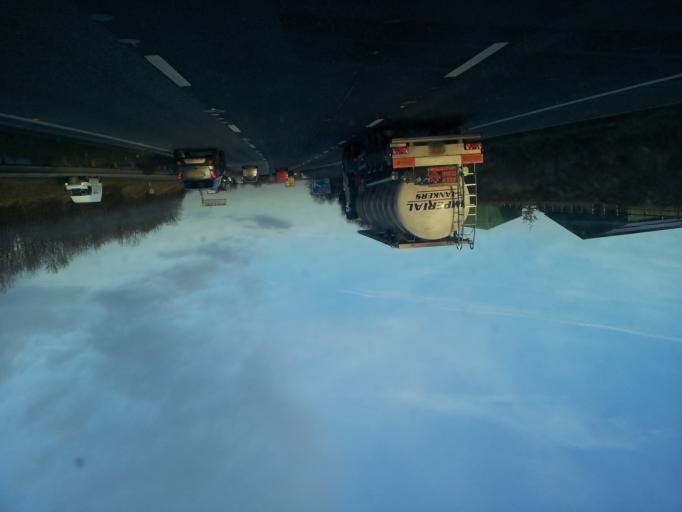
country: GB
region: England
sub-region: City and Borough of Wakefield
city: Castleford
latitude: 53.7056
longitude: -1.3623
